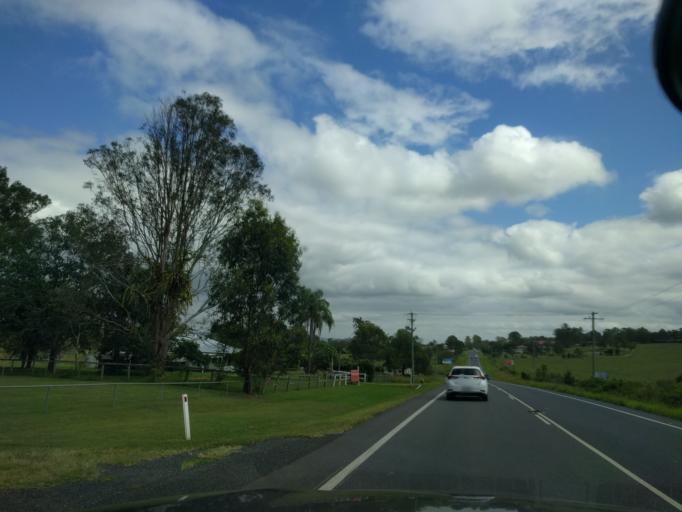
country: AU
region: Queensland
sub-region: Logan
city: Cedar Vale
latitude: -27.8997
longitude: 152.9747
